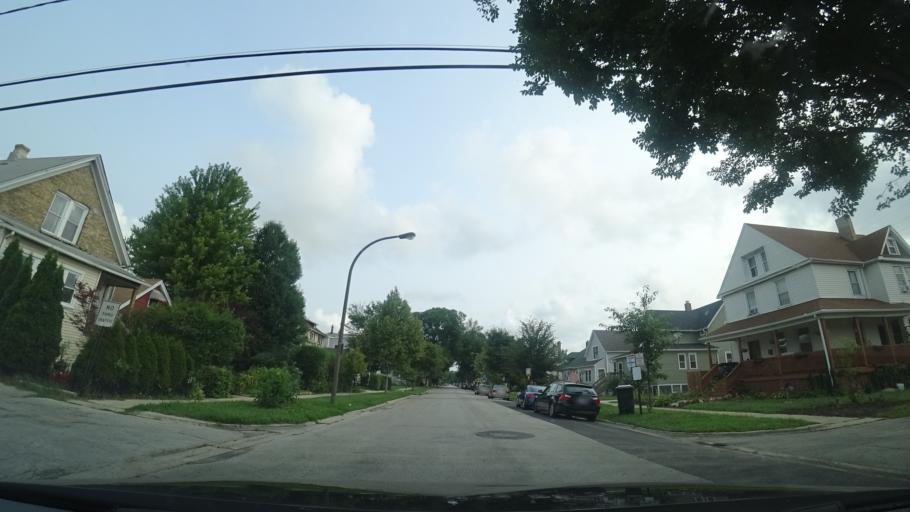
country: US
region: Illinois
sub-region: Cook County
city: Evanston
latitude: 42.0489
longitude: -87.6974
